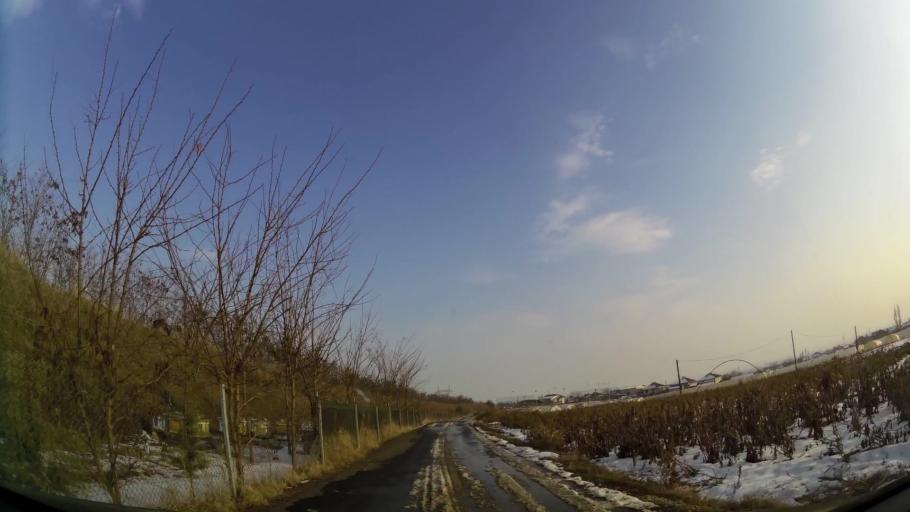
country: MK
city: Creshevo
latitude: 42.0331
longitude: 21.5237
